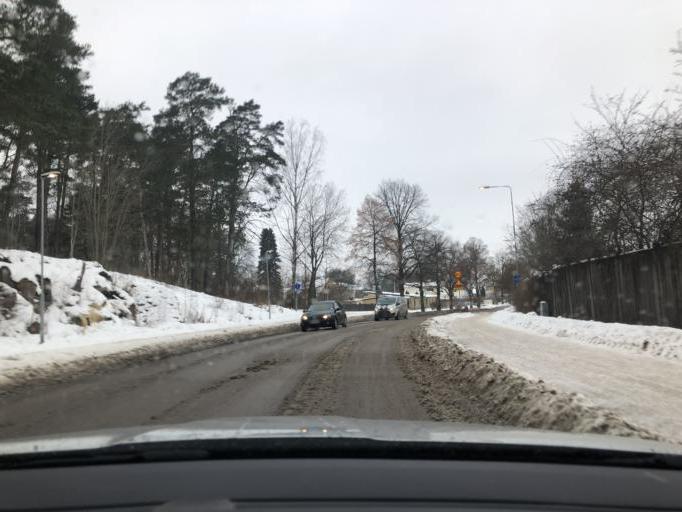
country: SE
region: Uppsala
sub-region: Uppsala Kommun
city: Uppsala
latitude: 59.8468
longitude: 17.6242
